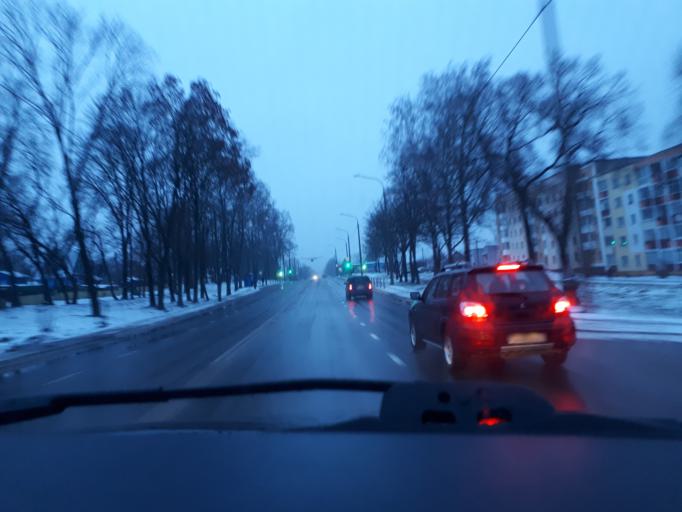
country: BY
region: Vitebsk
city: Vitebsk
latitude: 55.2259
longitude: 30.1180
